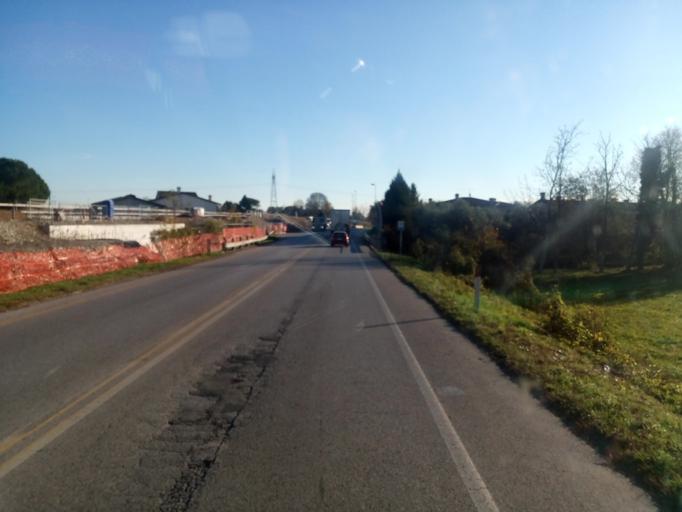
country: IT
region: Veneto
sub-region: Provincia di Vicenza
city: Cartigliano
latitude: 45.7379
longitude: 11.7048
